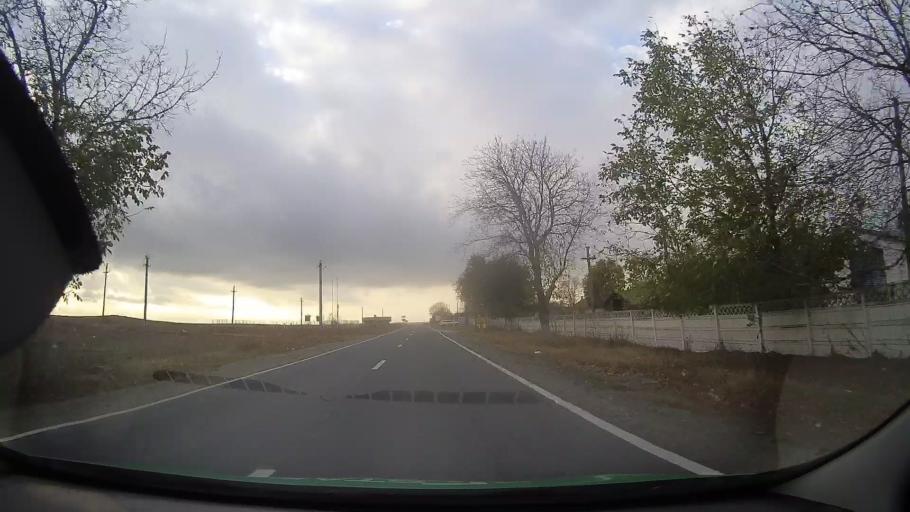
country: RO
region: Constanta
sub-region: Comuna Adamclisi
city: Adamclisi
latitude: 44.0884
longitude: 27.9670
